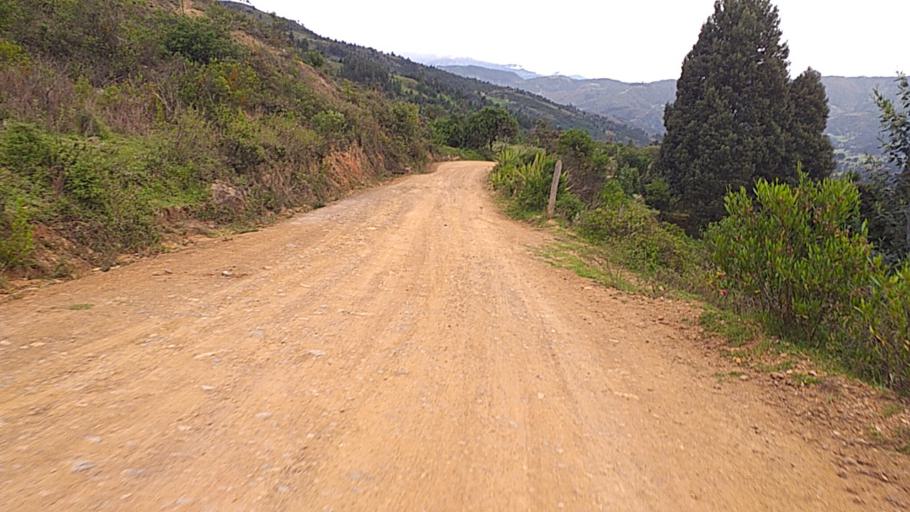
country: CO
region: Boyaca
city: Floresta
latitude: 5.8827
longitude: -72.9108
